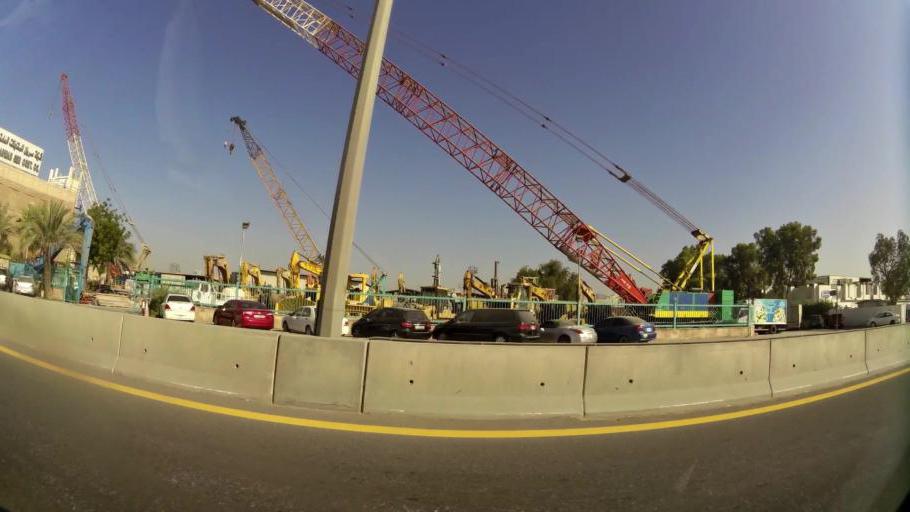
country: AE
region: Ash Shariqah
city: Sharjah
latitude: 25.3054
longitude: 55.4017
